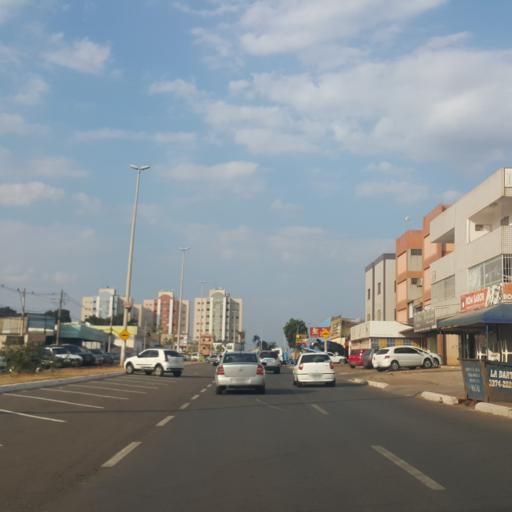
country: BR
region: Federal District
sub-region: Brasilia
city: Brasilia
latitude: -15.8710
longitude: -48.0281
